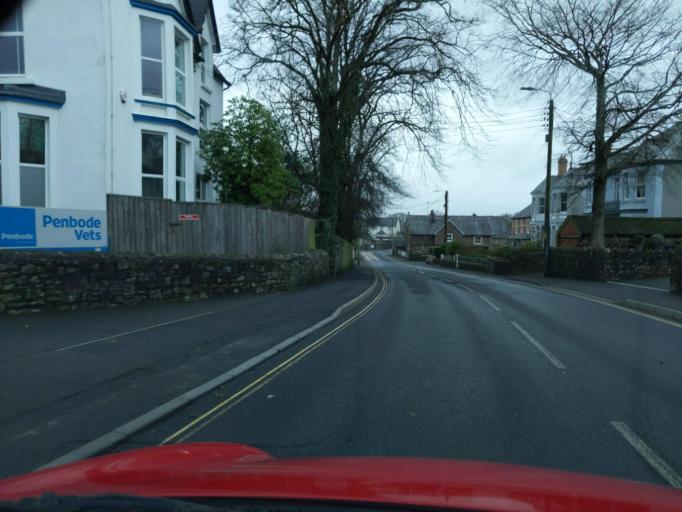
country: GB
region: England
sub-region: Devon
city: Holsworthy
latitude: 50.8118
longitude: -4.3516
